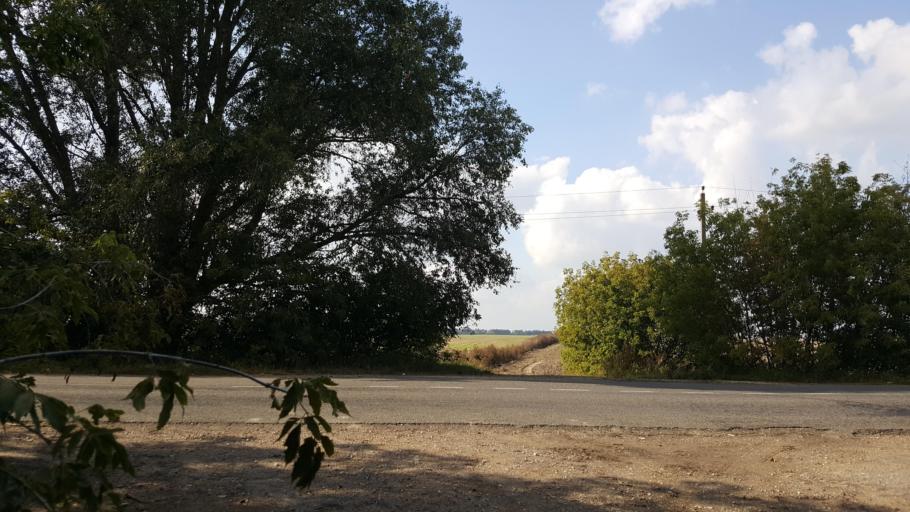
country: BY
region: Brest
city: Kamyanyets
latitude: 52.4230
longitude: 23.8088
